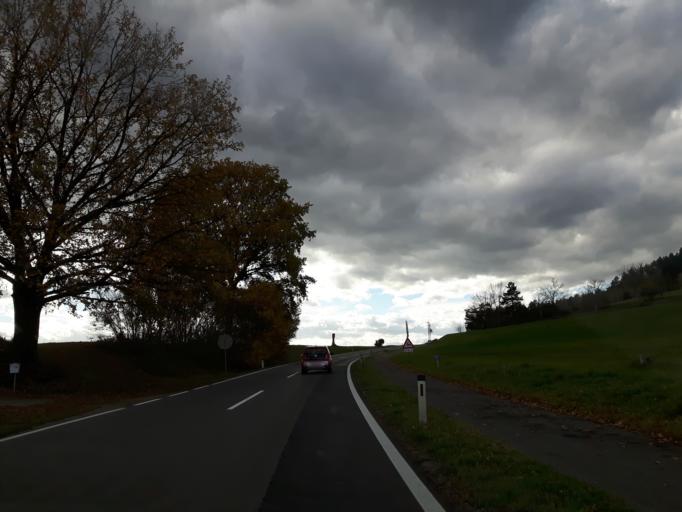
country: AT
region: Styria
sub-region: Politischer Bezirk Suedoststeiermark
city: Kirchbach in Steiermark
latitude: 46.9102
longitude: 15.6717
